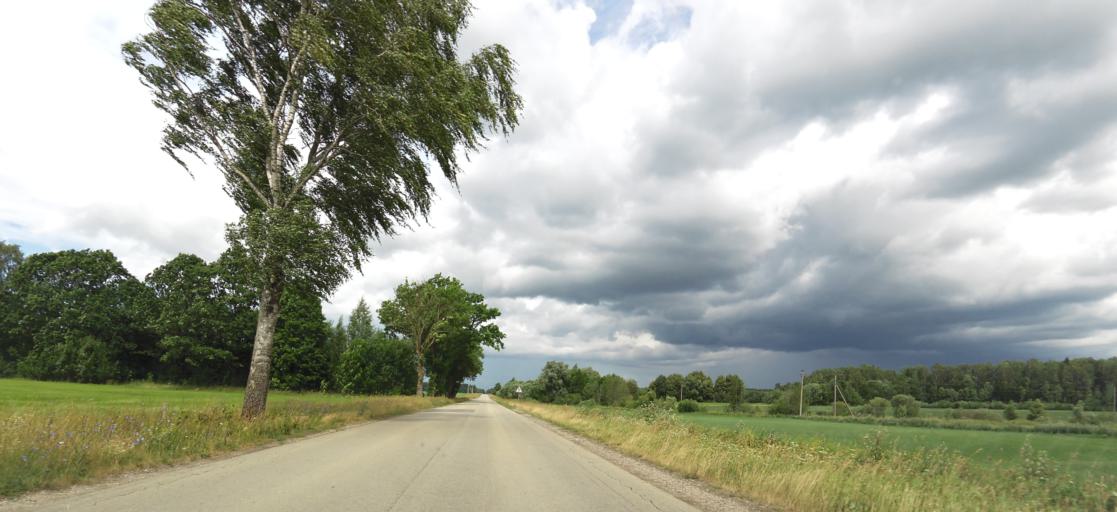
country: LT
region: Panevezys
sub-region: Birzai
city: Birzai
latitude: 56.3340
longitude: 24.8034
